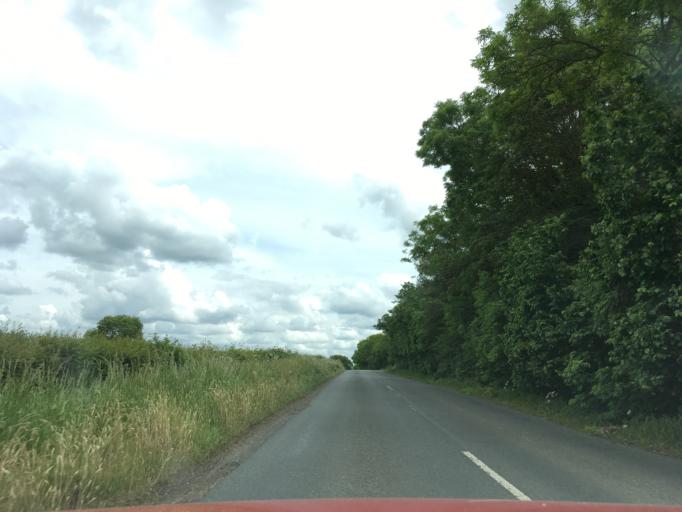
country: GB
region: England
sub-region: Wiltshire
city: Charlton
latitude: 51.5657
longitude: -2.0192
